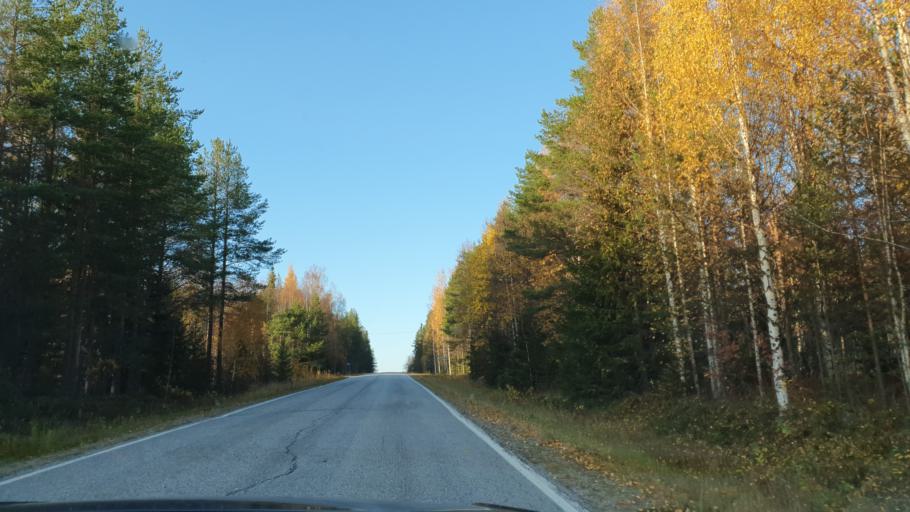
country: FI
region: Kainuu
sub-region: Kehys-Kainuu
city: Kuhmo
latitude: 64.3600
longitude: 29.4889
